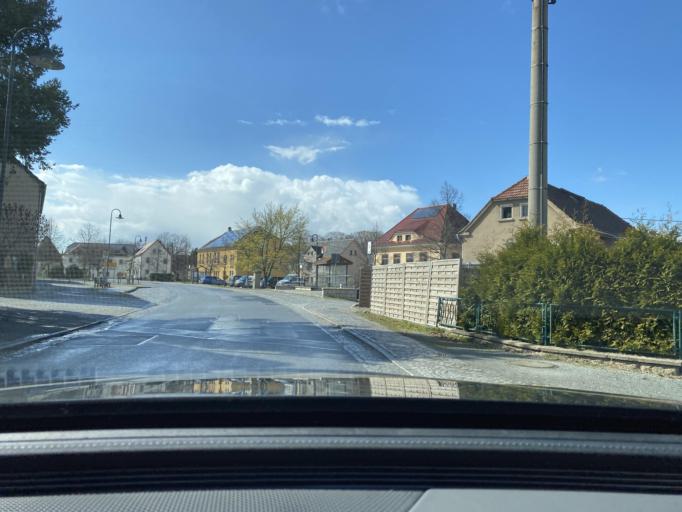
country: DE
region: Saxony
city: Radibor
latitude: 51.2447
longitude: 14.3990
